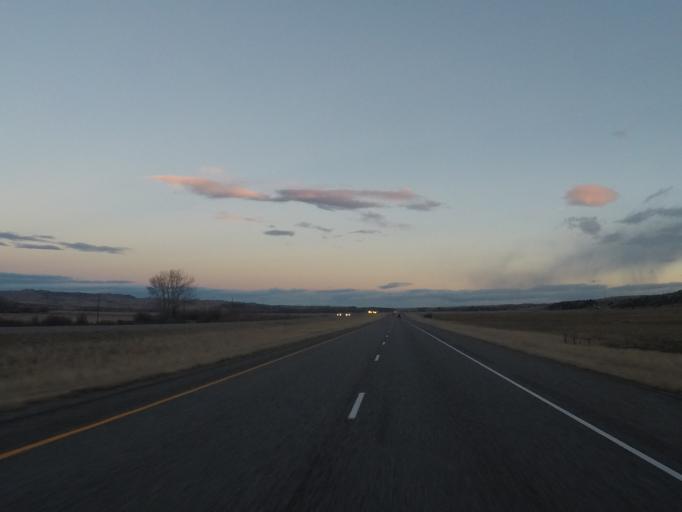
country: US
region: Montana
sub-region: Sweet Grass County
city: Big Timber
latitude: 45.7920
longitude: -109.8308
